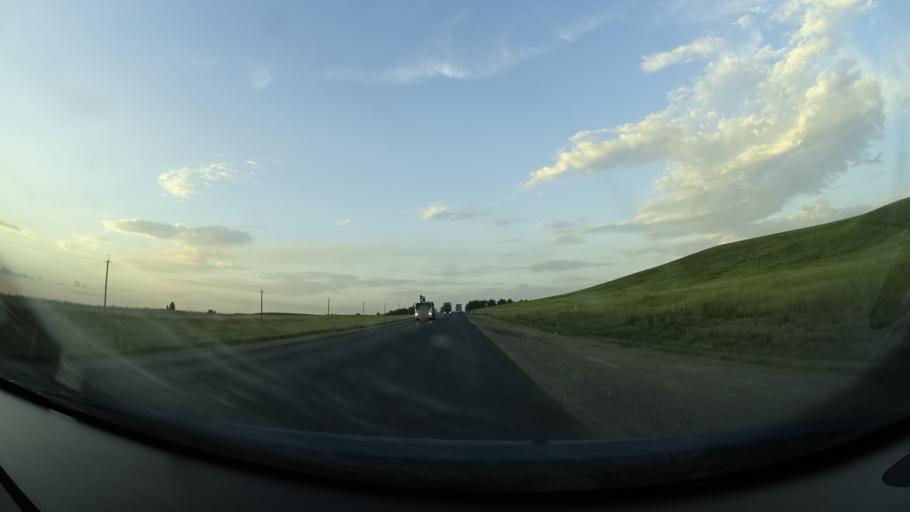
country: RU
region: Orenburg
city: Severnoye
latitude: 54.1447
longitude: 52.6088
